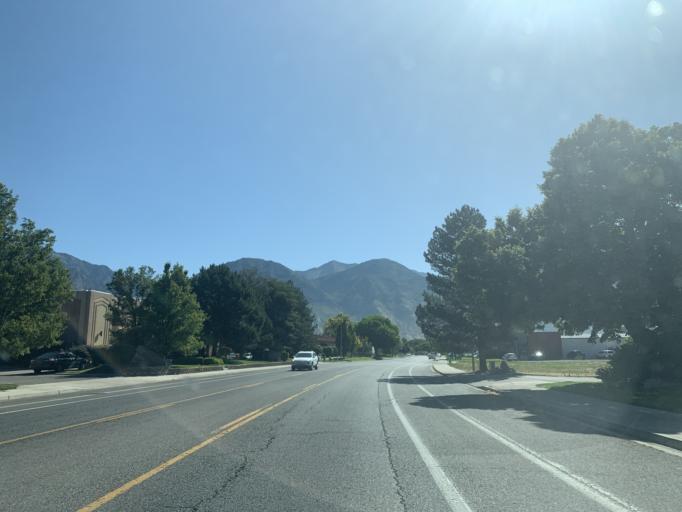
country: US
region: Utah
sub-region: Utah County
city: Provo
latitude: 40.2452
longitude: -111.6876
